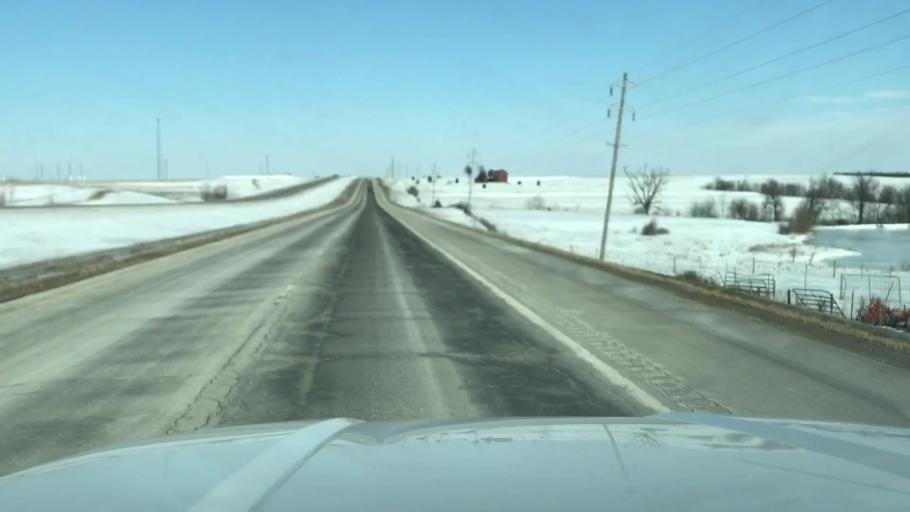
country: US
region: Missouri
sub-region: Nodaway County
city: Maryville
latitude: 40.2200
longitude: -94.8678
